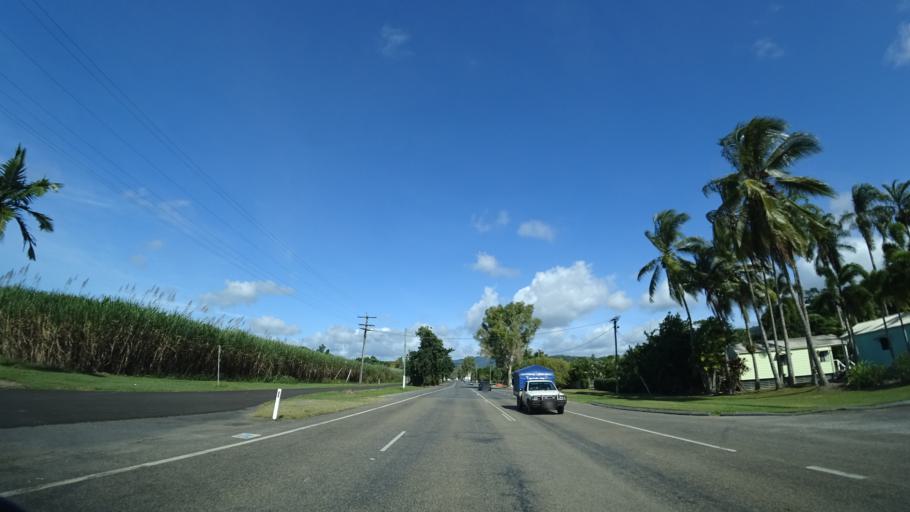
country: AU
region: Queensland
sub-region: Cairns
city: Port Douglas
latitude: -16.4701
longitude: 145.3732
